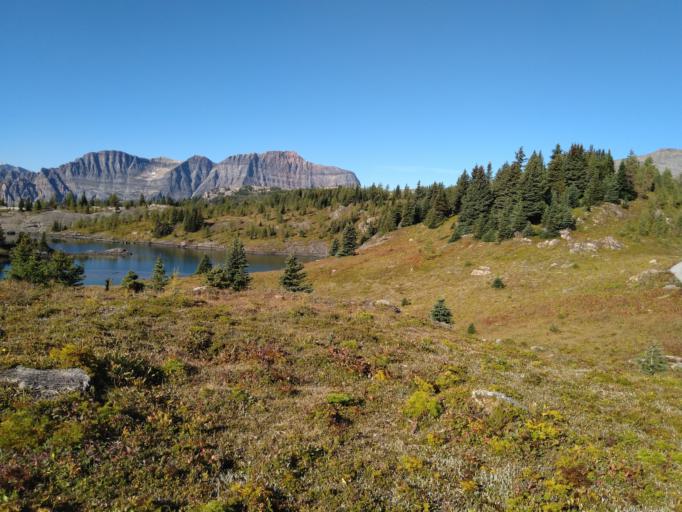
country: CA
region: Alberta
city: Banff
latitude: 51.0644
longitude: -115.7813
